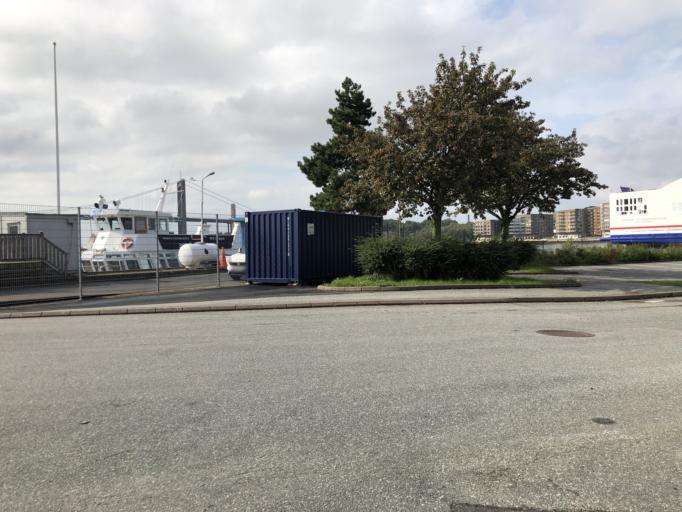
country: SE
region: Vaestra Goetaland
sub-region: Goteborg
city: Majorna
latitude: 57.6935
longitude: 11.9142
